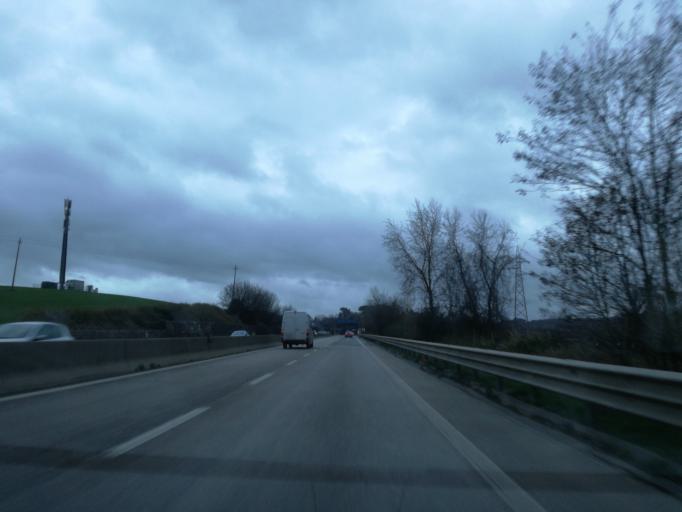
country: IT
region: Umbria
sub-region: Provincia di Perugia
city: Via Lippia
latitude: 43.0936
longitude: 12.4751
